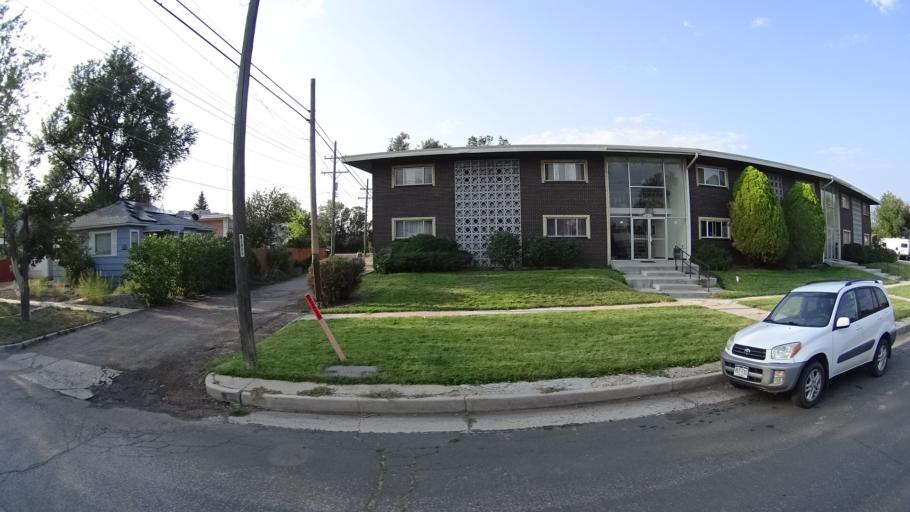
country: US
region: Colorado
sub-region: El Paso County
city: Colorado Springs
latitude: 38.8345
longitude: -104.7986
